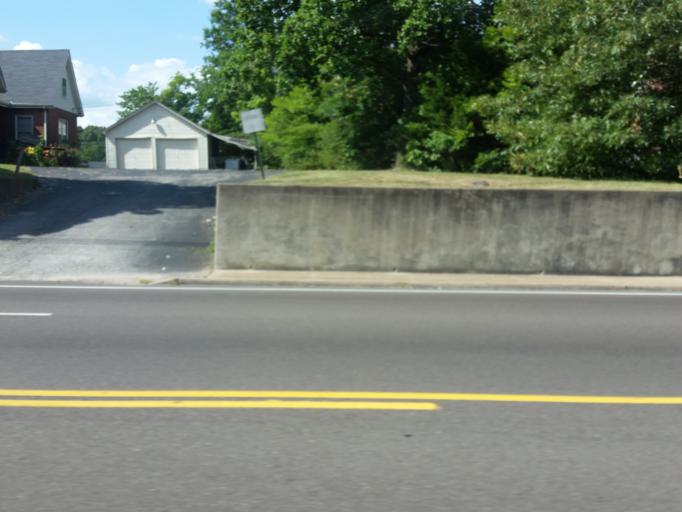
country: US
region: Tennessee
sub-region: Henderson County
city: Lexington
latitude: 35.6543
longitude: -88.3993
